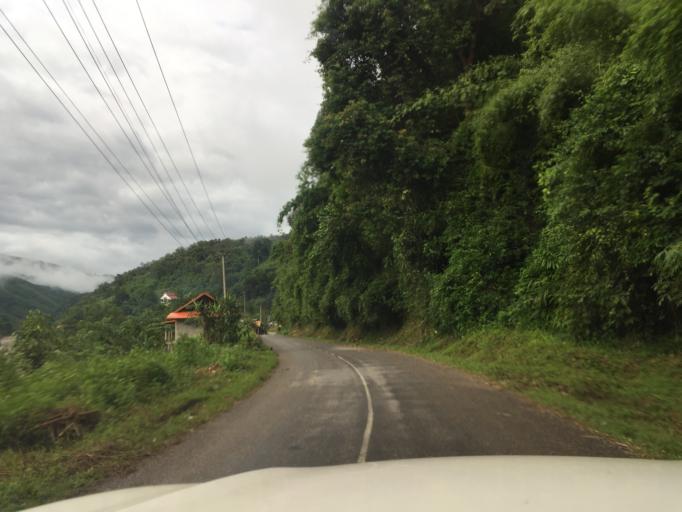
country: LA
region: Oudomxai
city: Muang La
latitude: 21.0577
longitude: 102.2412
